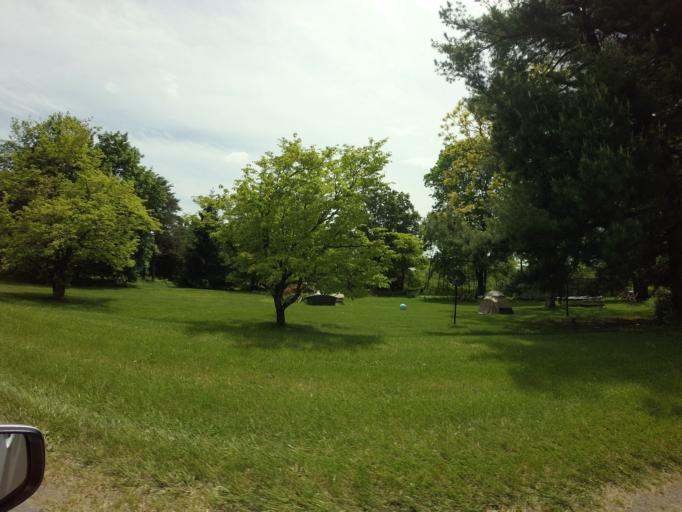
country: US
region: Maryland
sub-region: Frederick County
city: Woodsboro
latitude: 39.5216
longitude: -77.2674
